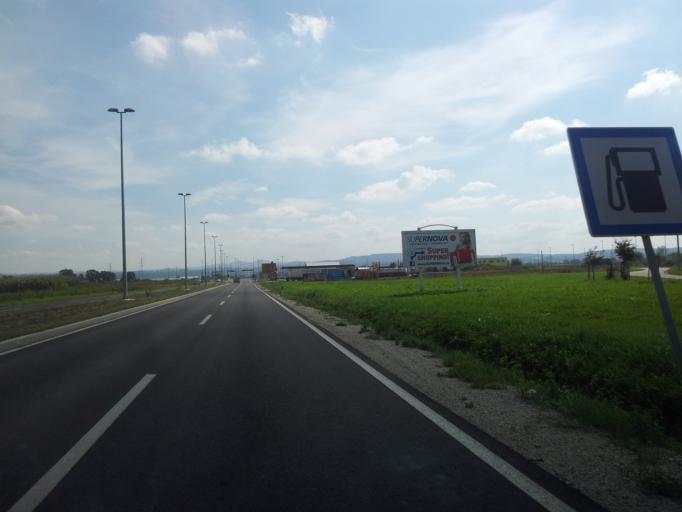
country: HR
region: Varazdinska
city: Varazdin
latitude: 46.2846
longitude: 16.3556
